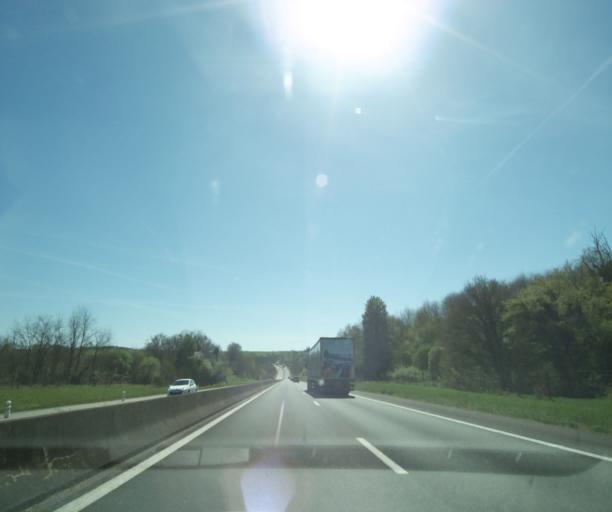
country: FR
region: Limousin
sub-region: Departement de la Haute-Vienne
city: Boisseuil
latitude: 45.7374
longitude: 1.3403
